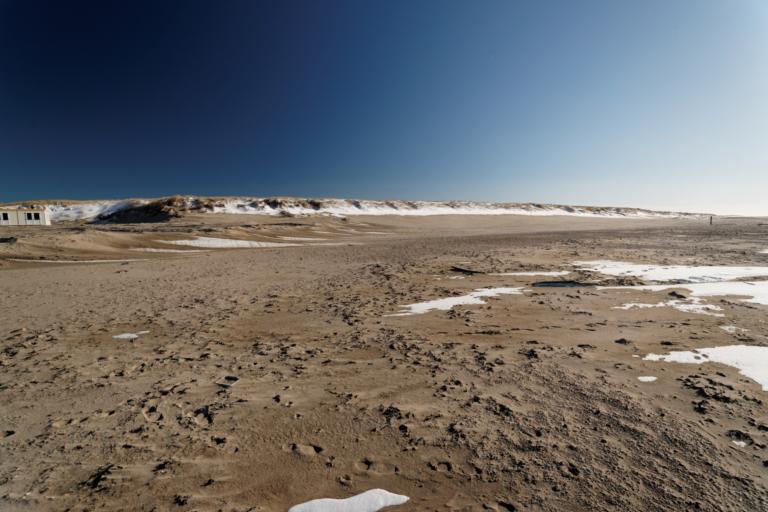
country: NL
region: North Holland
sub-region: Gemeente Texel
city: Den Burg
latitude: 53.1626
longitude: 4.8199
